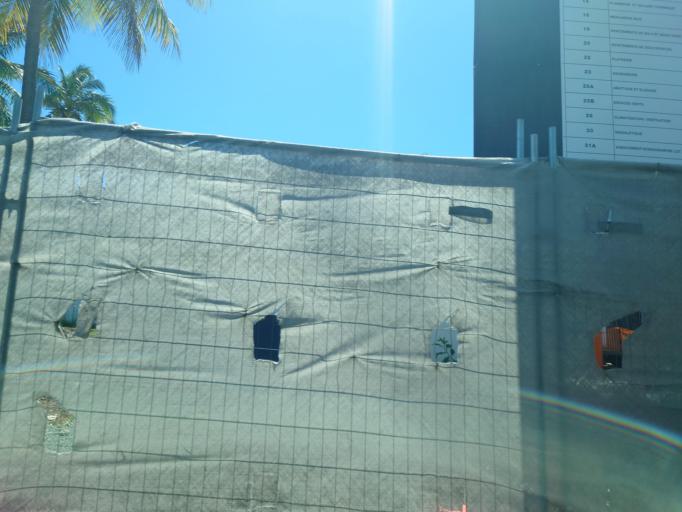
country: NC
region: South Province
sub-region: Noumea
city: Noumea
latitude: -22.2760
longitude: 166.4430
